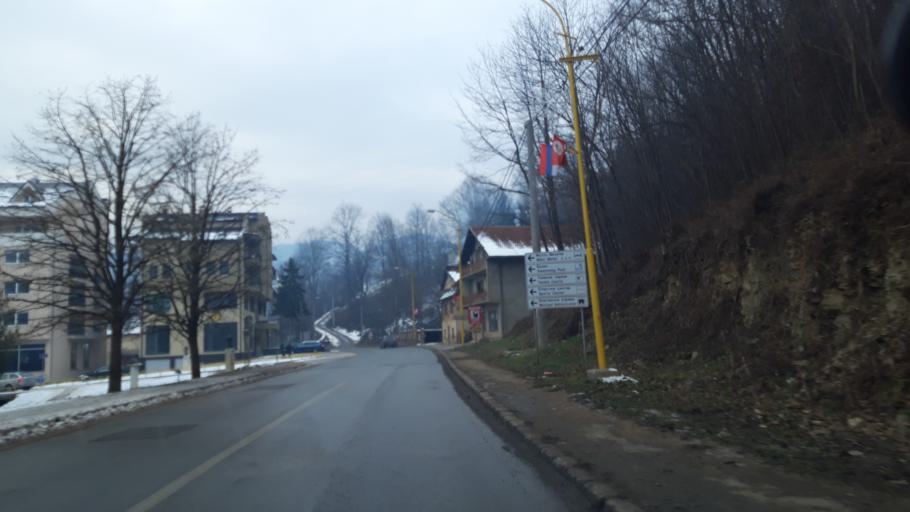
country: BA
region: Republika Srpska
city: Milici
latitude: 44.1691
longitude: 19.0749
